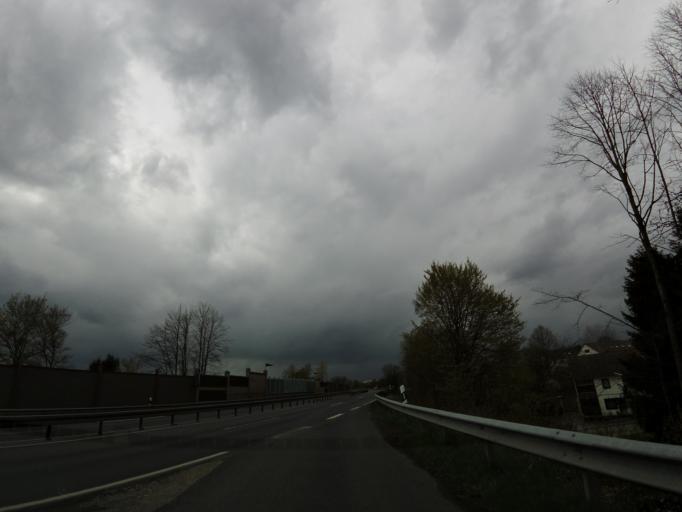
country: DE
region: Lower Saxony
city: Osterode am Harz
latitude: 51.7441
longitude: 10.2293
